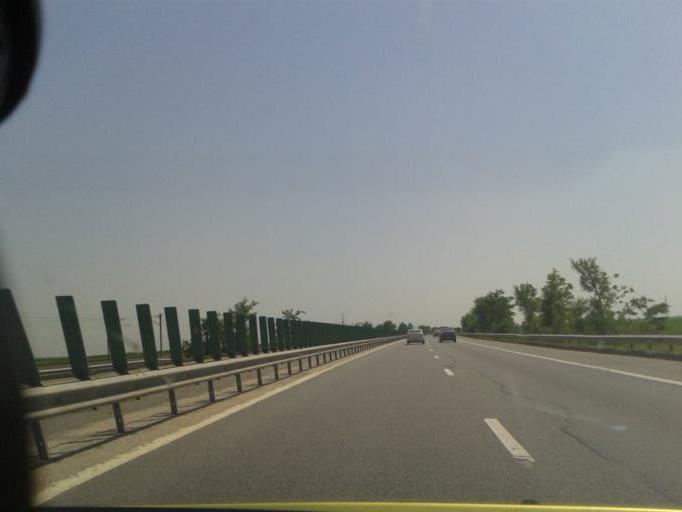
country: RO
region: Calarasi
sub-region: Comuna Nicolae Balcescu
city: Nicolae Balcescu
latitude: 44.4432
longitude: 26.7714
